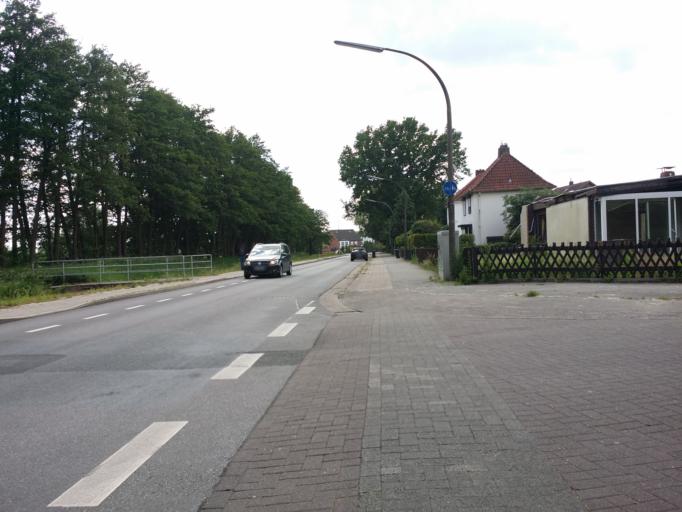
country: DE
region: Lower Saxony
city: Delmenhorst
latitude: 53.0412
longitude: 8.6130
